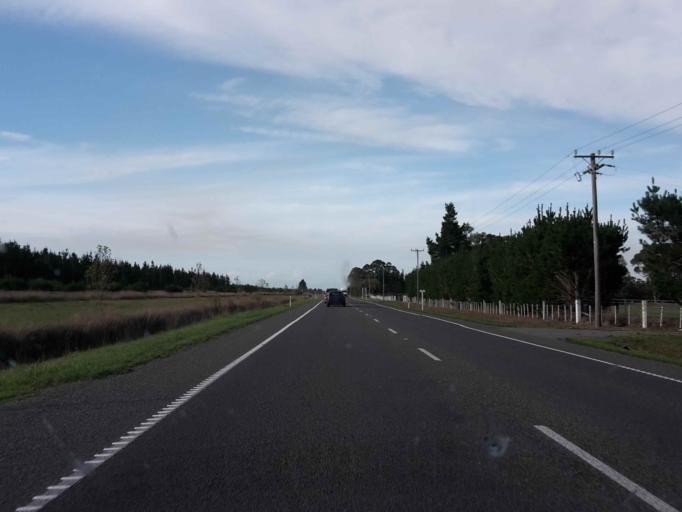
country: NZ
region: Canterbury
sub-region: Ashburton District
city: Tinwald
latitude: -43.9715
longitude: 171.6254
